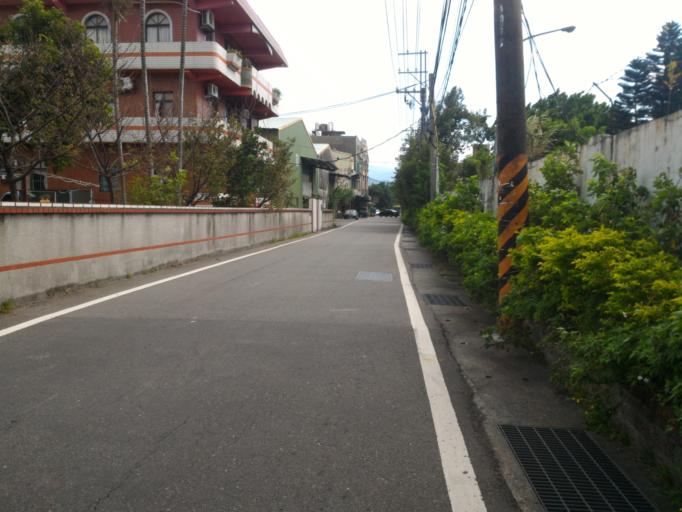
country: TW
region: Taipei
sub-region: Taipei
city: Banqiao
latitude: 24.9645
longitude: 121.3995
